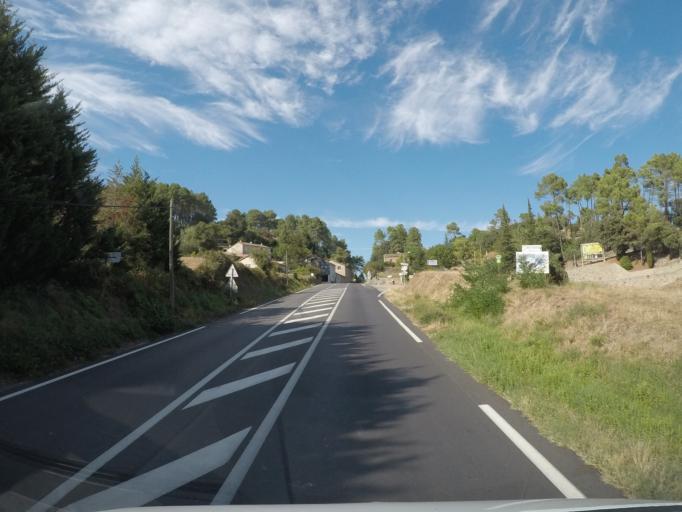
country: FR
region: Languedoc-Roussillon
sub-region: Departement du Gard
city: Anduze
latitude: 44.0705
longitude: 3.9693
